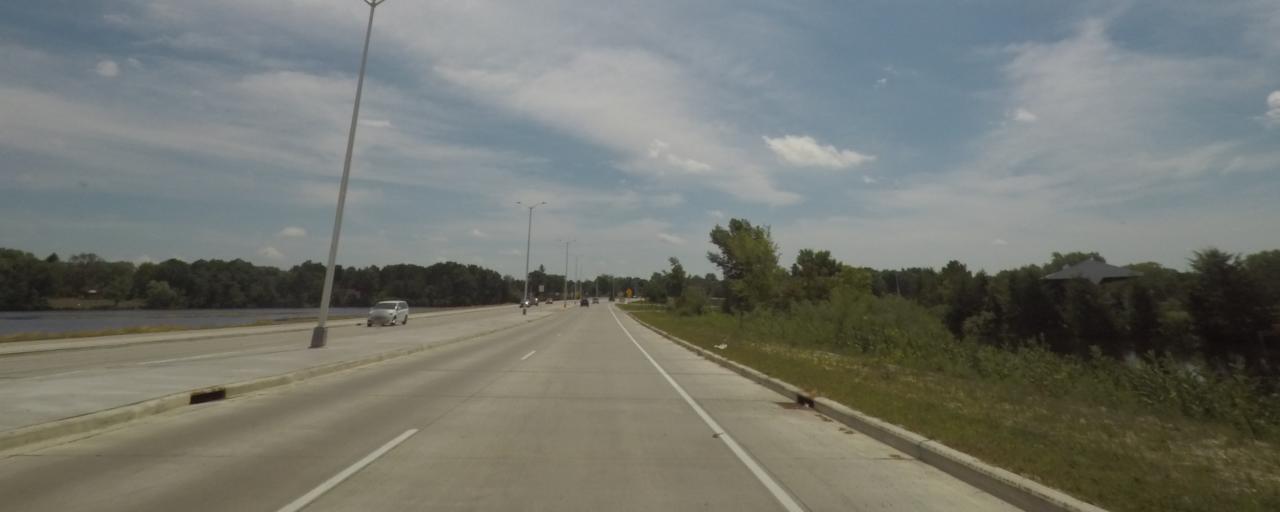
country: US
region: Wisconsin
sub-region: Portage County
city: Whiting
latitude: 44.4954
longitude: -89.5567
